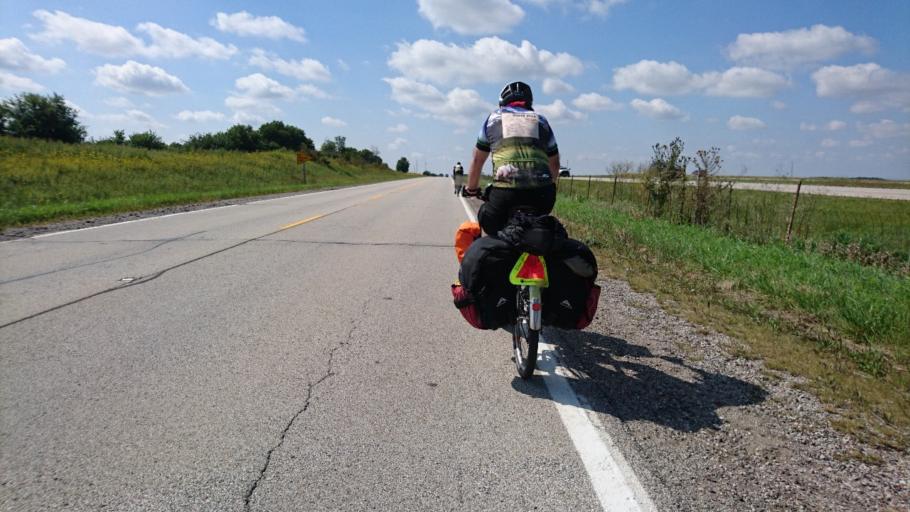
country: US
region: Illinois
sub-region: McLean County
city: Lexington
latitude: 40.5964
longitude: -88.8508
